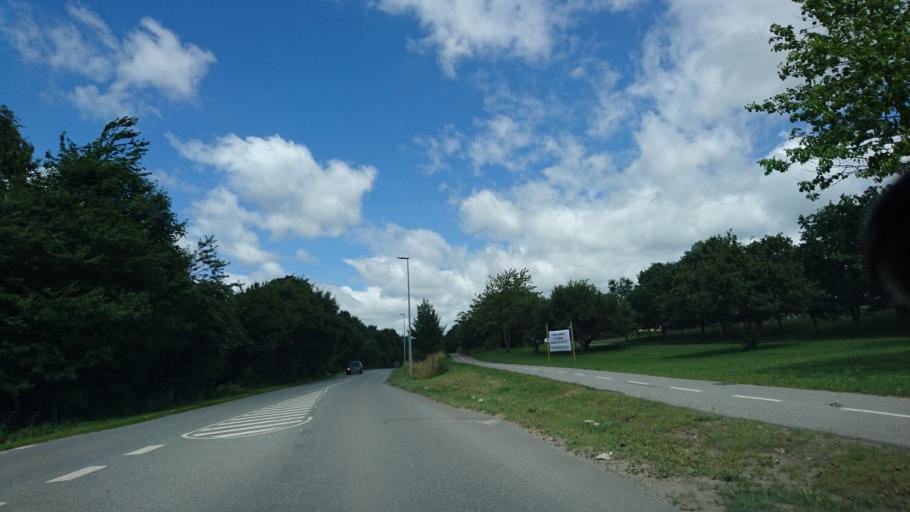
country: DK
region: Central Jutland
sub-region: Arhus Kommune
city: Stavtrup
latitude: 56.1709
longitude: 10.1194
